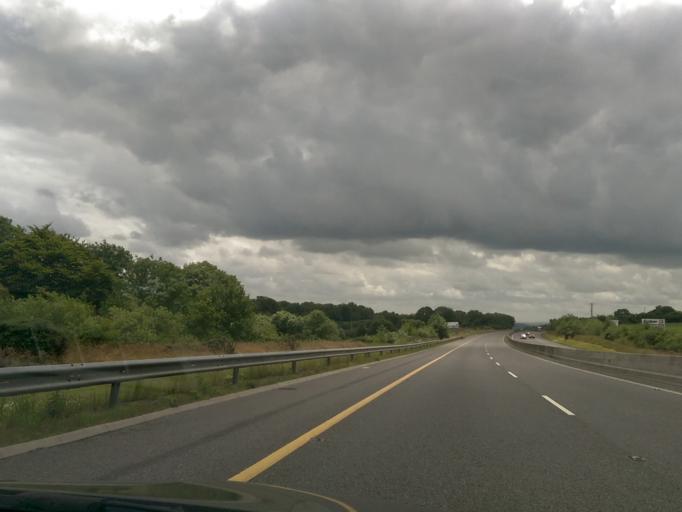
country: IE
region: Munster
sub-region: County Cork
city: Mitchelstown
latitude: 52.2068
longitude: -8.2747
